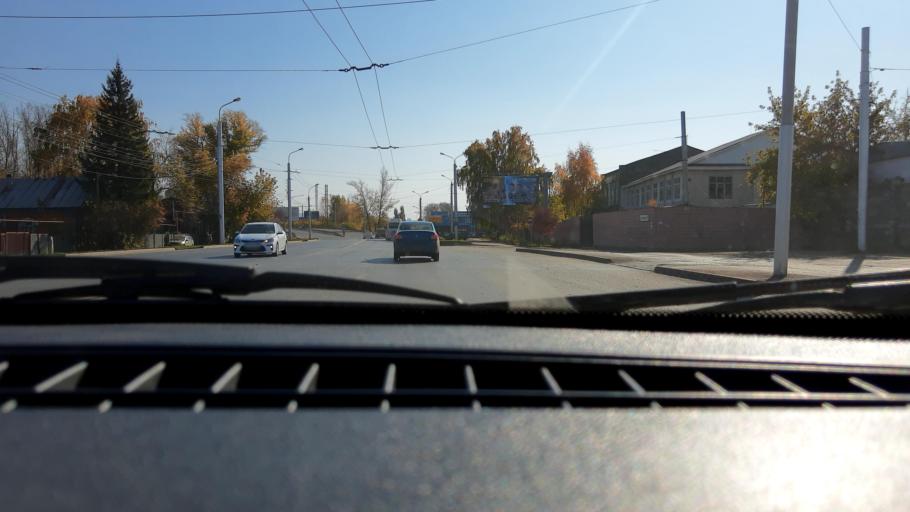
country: RU
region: Bashkortostan
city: Mikhaylovka
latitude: 54.7781
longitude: 55.8905
